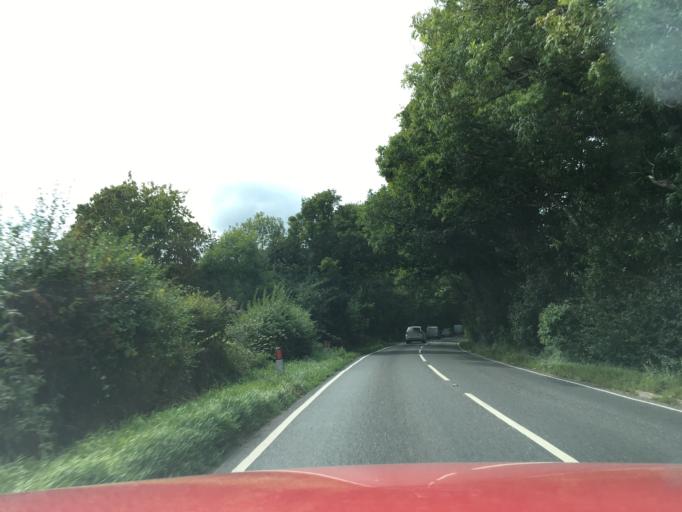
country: GB
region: England
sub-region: Kent
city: Paddock Wood
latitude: 51.1096
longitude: 0.4181
